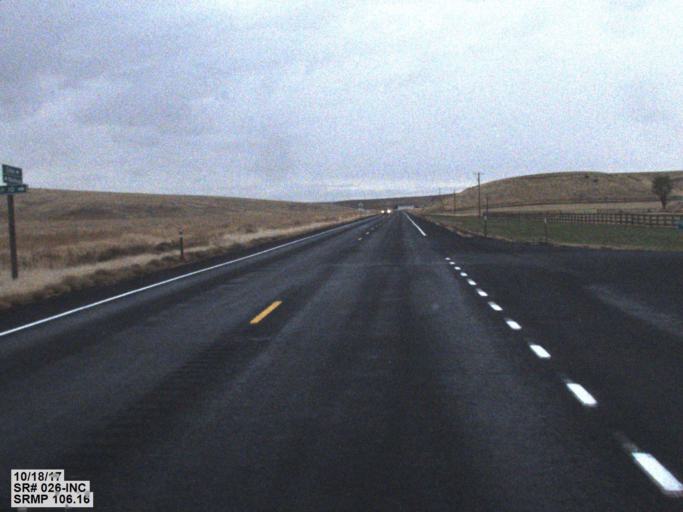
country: US
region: Washington
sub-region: Garfield County
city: Pomeroy
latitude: 46.7973
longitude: -117.8676
